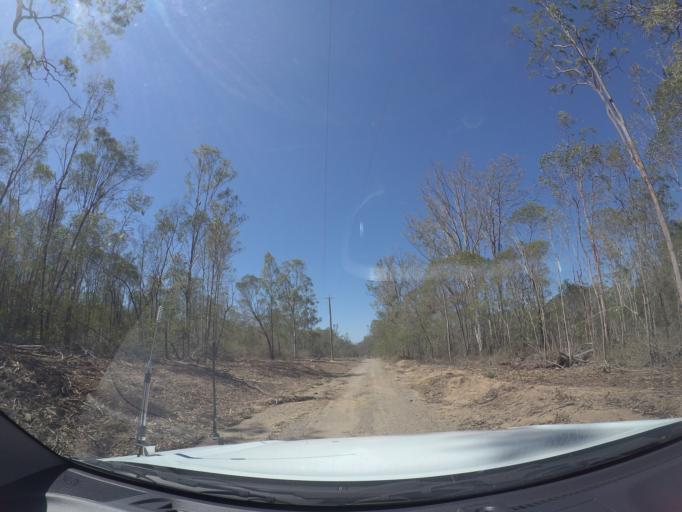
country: AU
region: Queensland
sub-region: Logan
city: North Maclean
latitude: -27.7679
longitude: 152.9373
